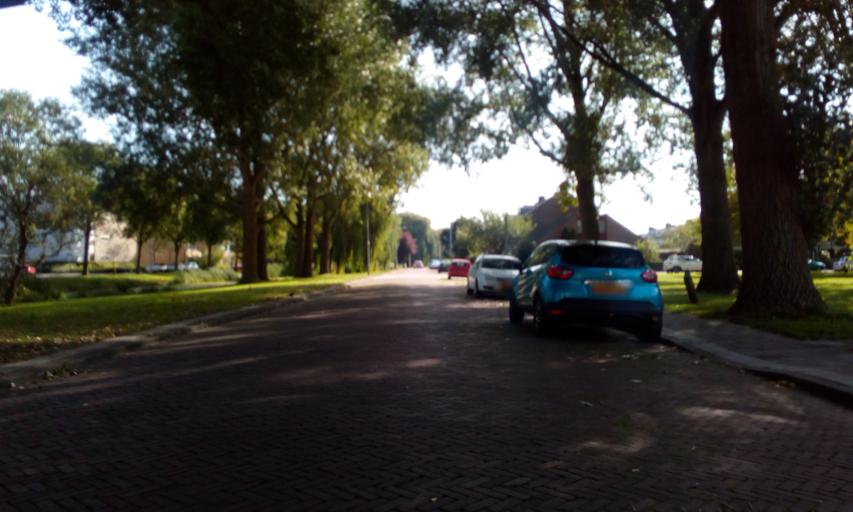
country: NL
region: South Holland
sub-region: Gemeente Voorschoten
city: Voorschoten
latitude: 52.1362
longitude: 4.4507
